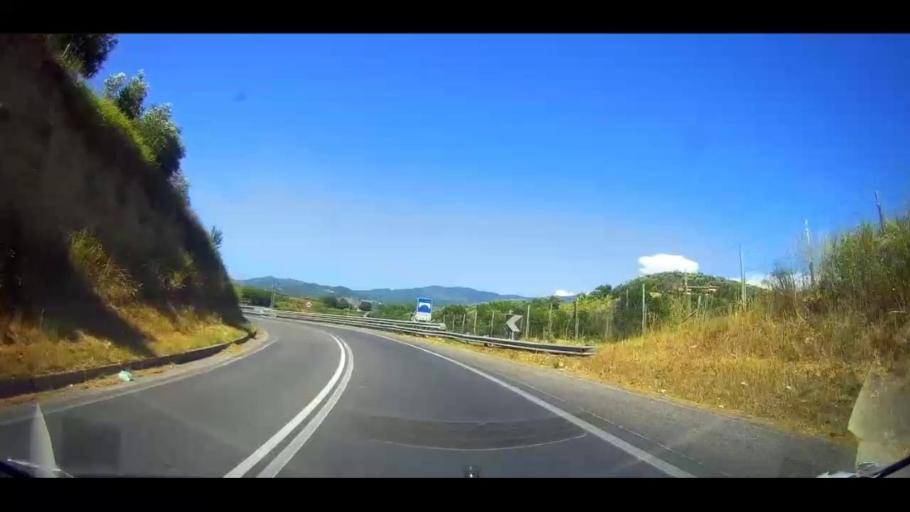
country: IT
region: Calabria
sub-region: Provincia di Cosenza
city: Cosenza
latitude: 39.2951
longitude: 16.2636
